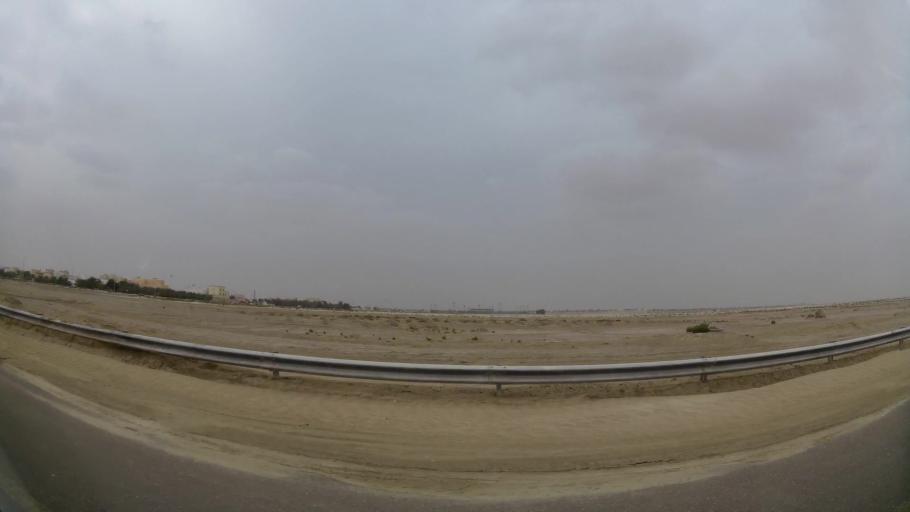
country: AE
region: Abu Dhabi
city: Abu Dhabi
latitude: 24.3774
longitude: 54.6752
